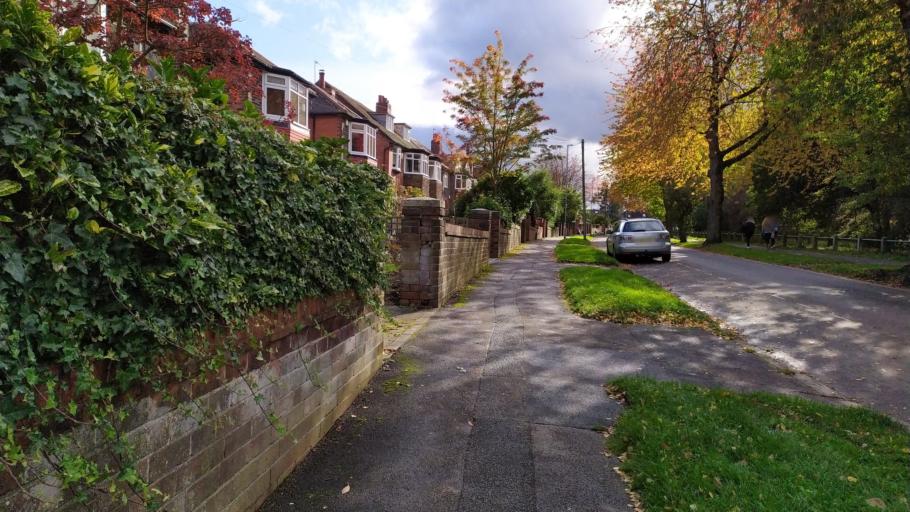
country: GB
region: England
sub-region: City and Borough of Leeds
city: Leeds
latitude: 53.8239
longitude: -1.5883
